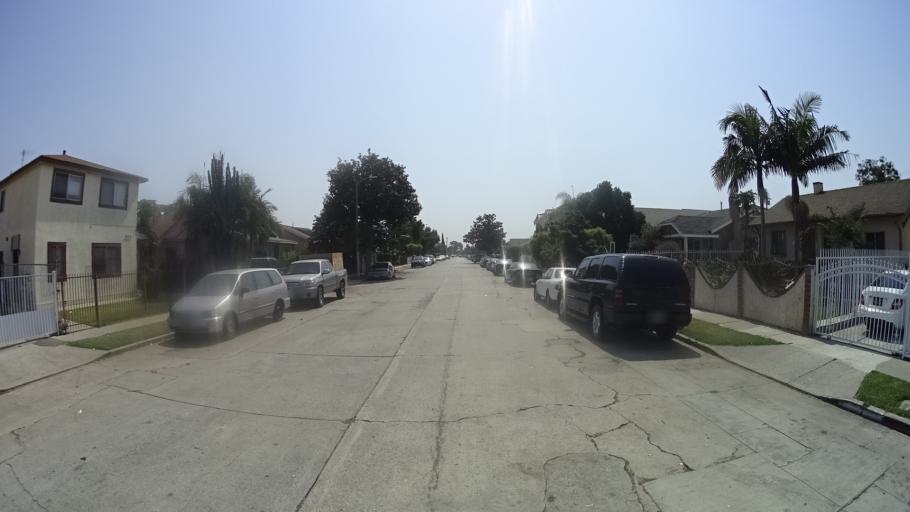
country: US
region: California
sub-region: Los Angeles County
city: Westmont
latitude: 33.9727
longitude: -118.2904
